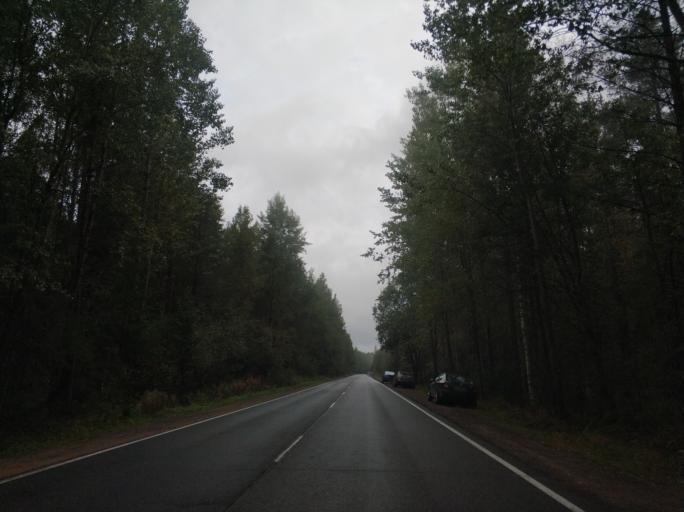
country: RU
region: Leningrad
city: Borisova Griva
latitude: 60.1566
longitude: 30.9288
